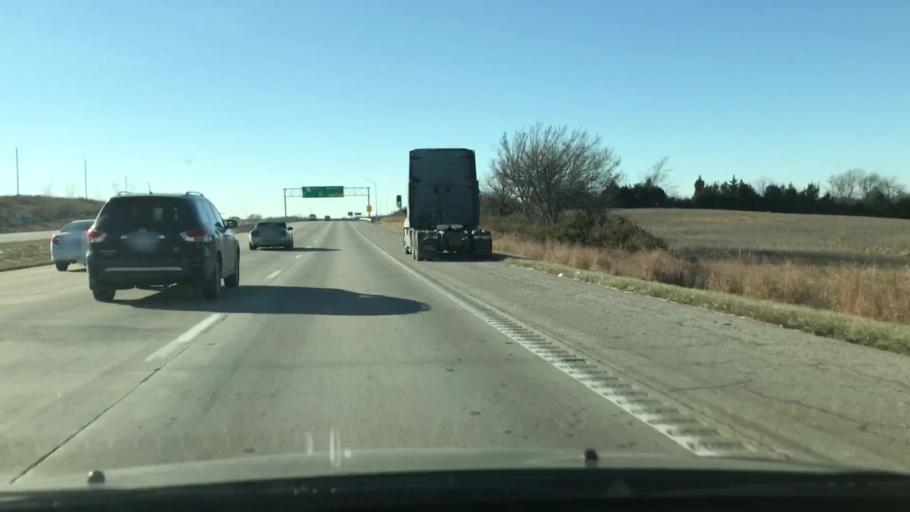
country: US
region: Missouri
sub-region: Jackson County
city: Grandview
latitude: 38.8585
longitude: -94.5397
